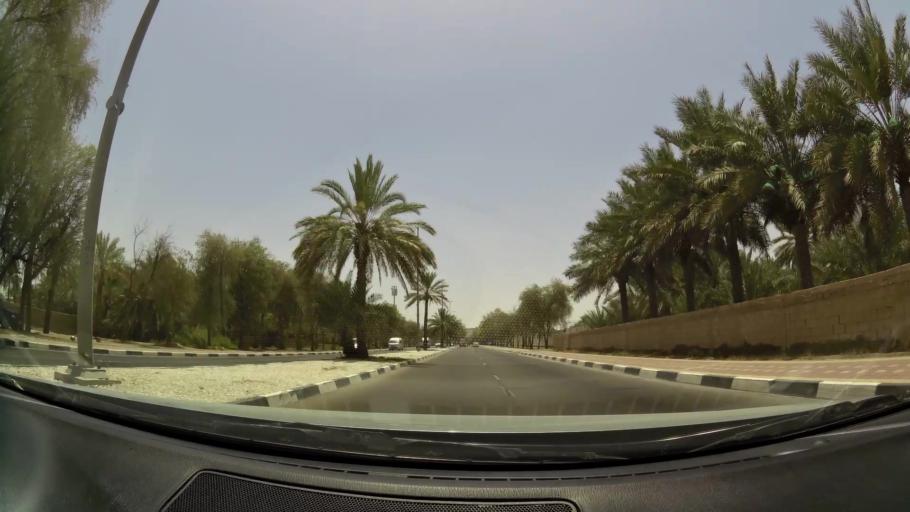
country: OM
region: Al Buraimi
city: Al Buraymi
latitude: 24.2648
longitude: 55.7593
